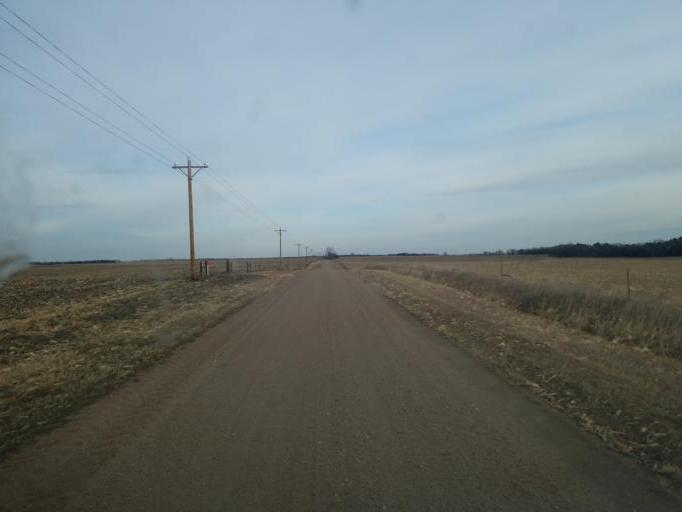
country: US
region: Nebraska
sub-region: Holt County
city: O'Neill
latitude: 42.4369
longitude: -98.3130
